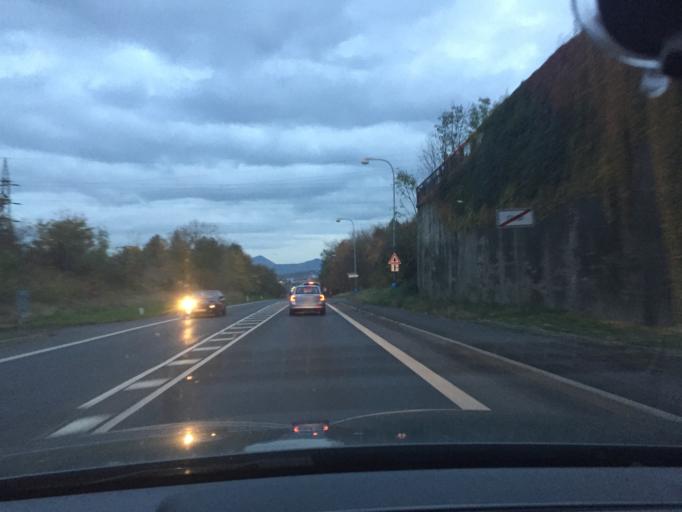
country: CZ
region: Ustecky
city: Novosedlice
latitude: 50.6520
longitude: 13.8102
